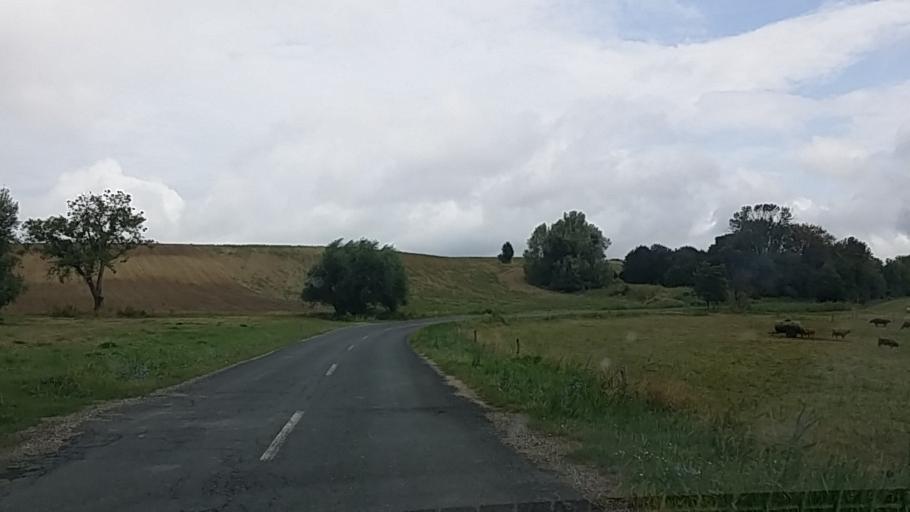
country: HU
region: Komarom-Esztergom
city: Tardos
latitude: 47.6340
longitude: 18.4534
